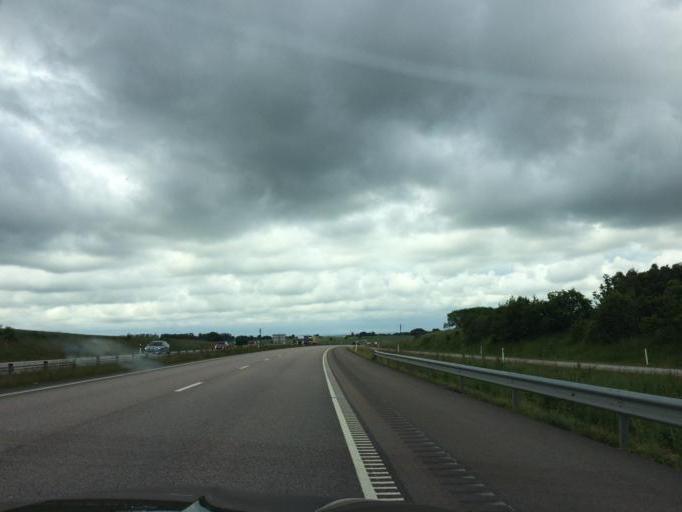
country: SE
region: Skane
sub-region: Helsingborg
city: Odakra
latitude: 56.0909
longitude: 12.7829
